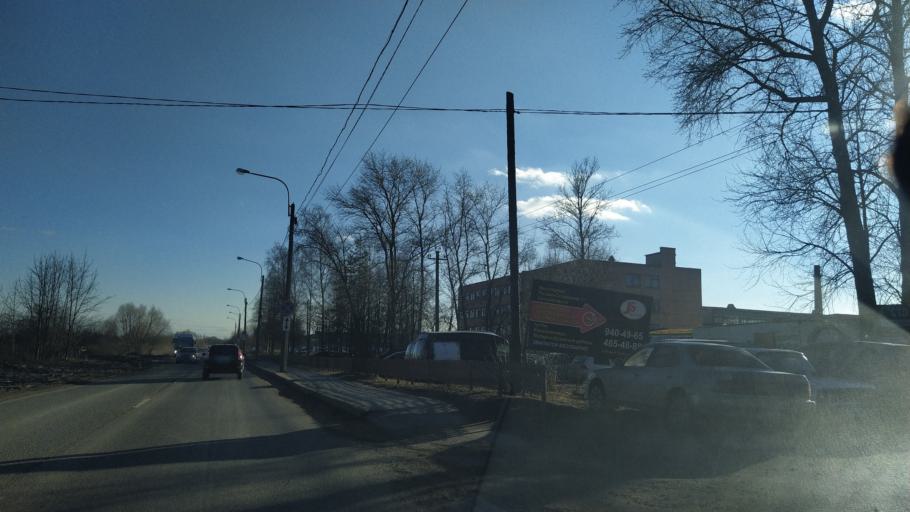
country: RU
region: St.-Petersburg
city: Pushkin
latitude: 59.6977
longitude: 30.3951
